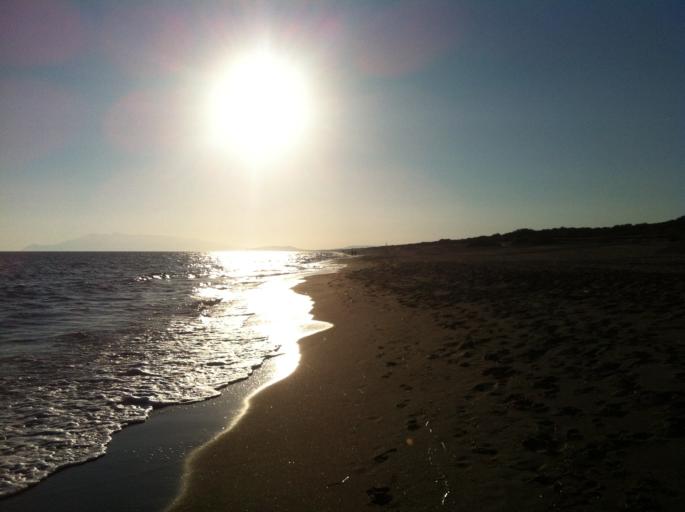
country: IT
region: Latium
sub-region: Provincia di Viterbo
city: Pescia Romana
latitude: 42.3820
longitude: 11.4350
